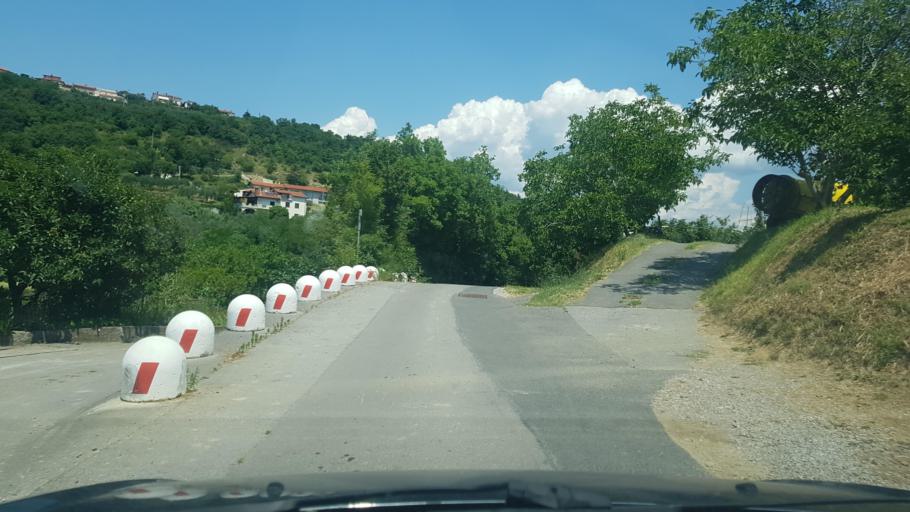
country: SI
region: Koper-Capodistria
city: Spodnje Skofije
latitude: 45.5743
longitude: 13.7875
